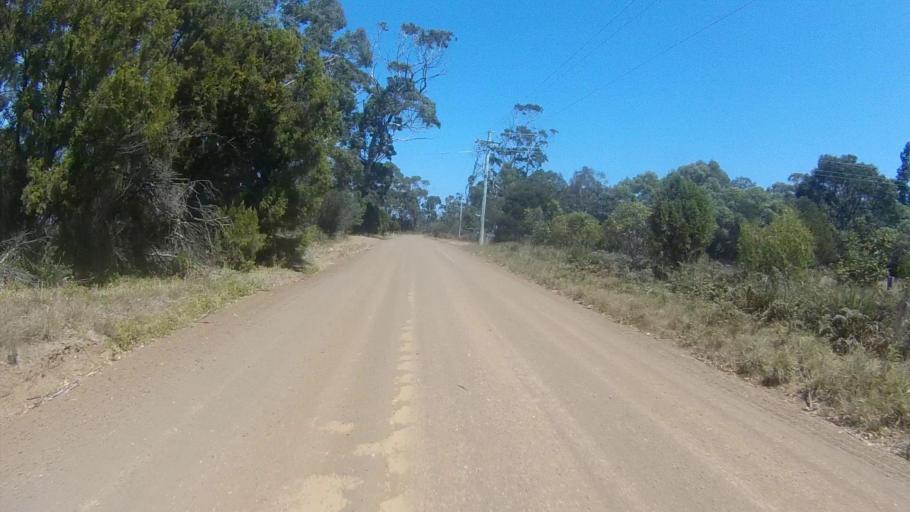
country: AU
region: Tasmania
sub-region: Sorell
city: Sorell
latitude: -42.8351
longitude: 147.8549
